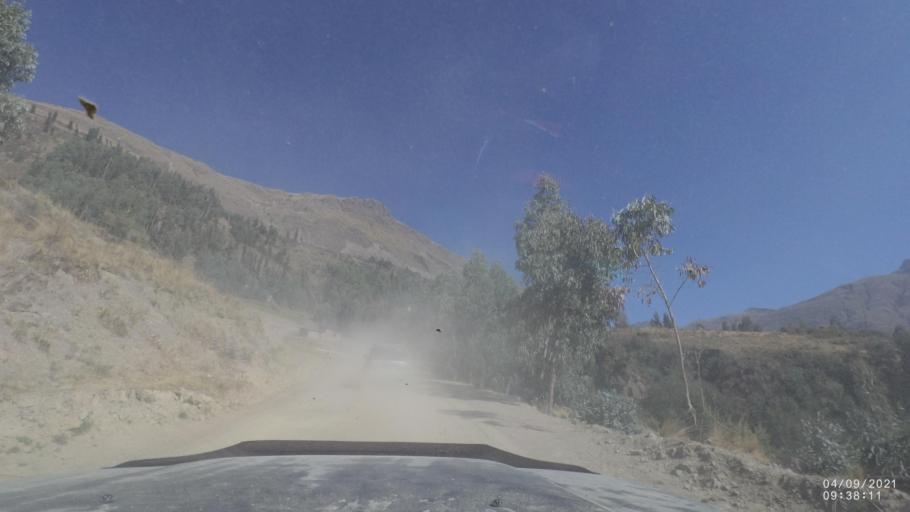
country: BO
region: Cochabamba
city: Sipe Sipe
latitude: -17.3457
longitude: -66.3831
